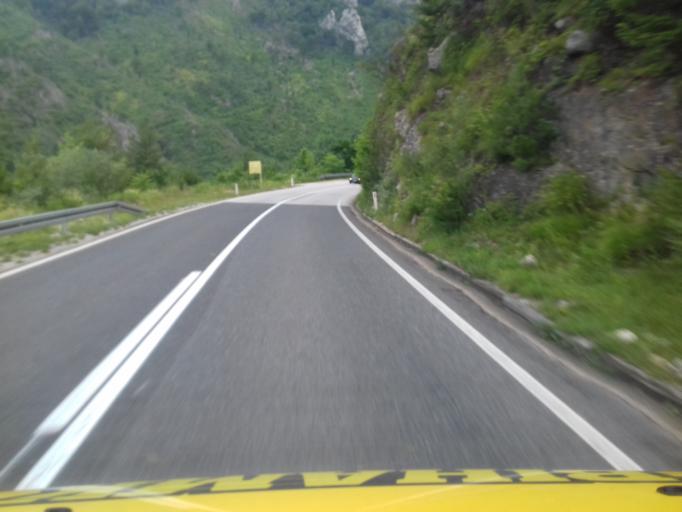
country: BA
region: Federation of Bosnia and Herzegovina
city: Jablanica
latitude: 43.6247
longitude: 17.7505
